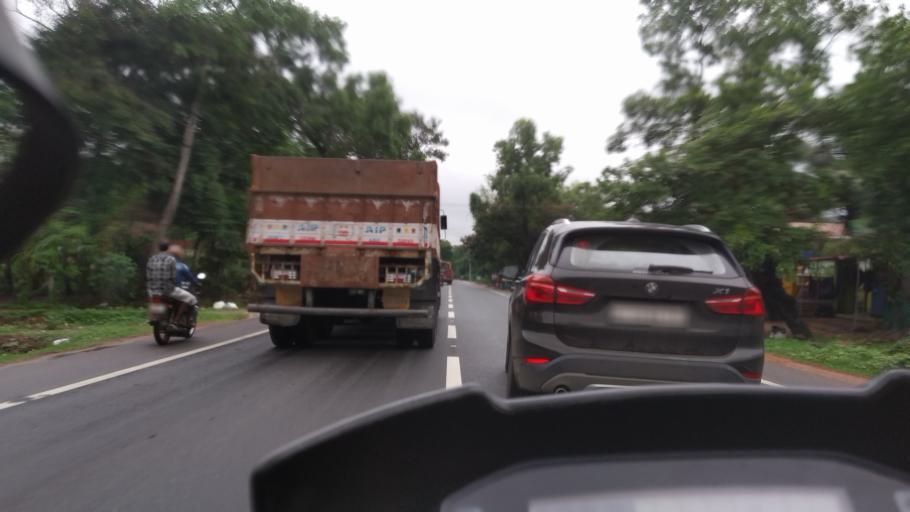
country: IN
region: Kerala
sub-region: Alappuzha
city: Mavelikara
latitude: 9.2961
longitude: 76.4341
